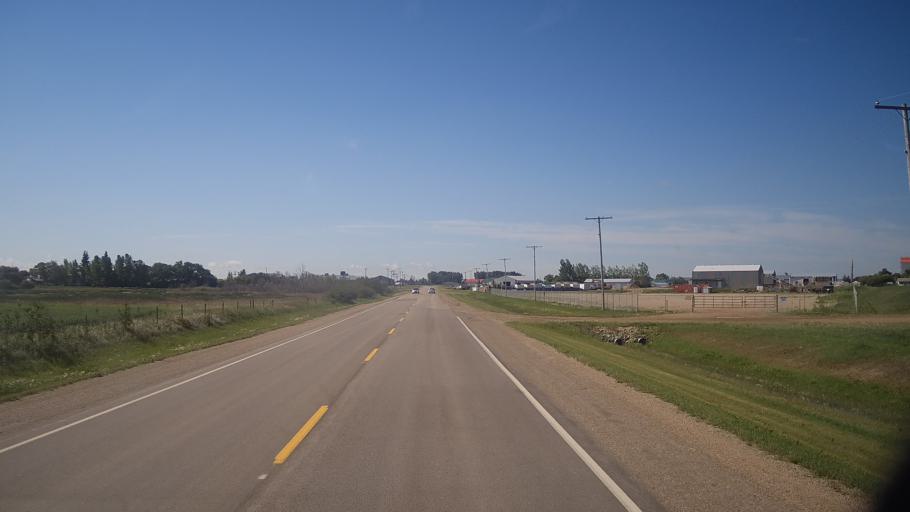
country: CA
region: Saskatchewan
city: Watrous
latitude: 51.6746
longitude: -105.4518
